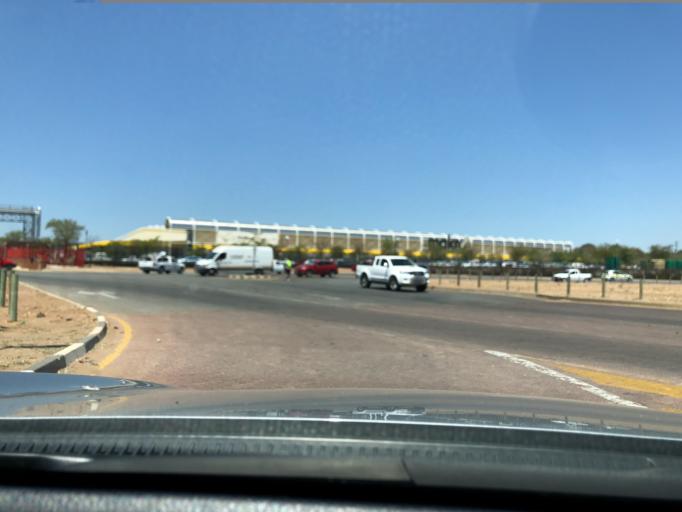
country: ZA
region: Limpopo
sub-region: Capricorn District Municipality
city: Polokwane
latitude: -23.8729
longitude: 29.4641
